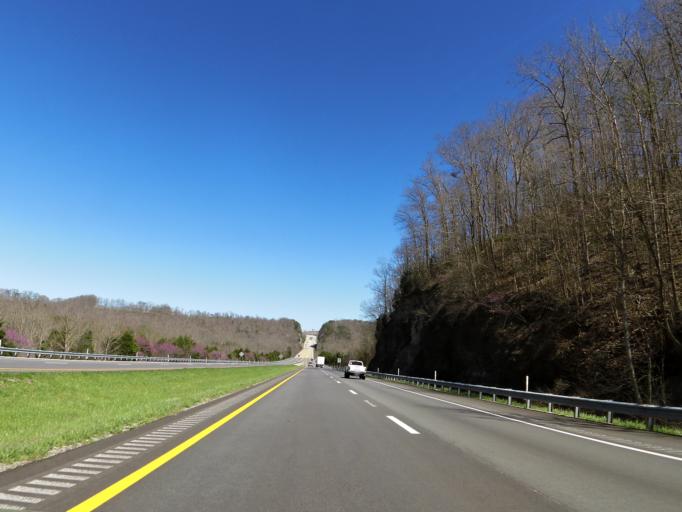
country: US
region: Kentucky
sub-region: Pulaski County
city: Somerset
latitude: 37.0965
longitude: -84.7000
